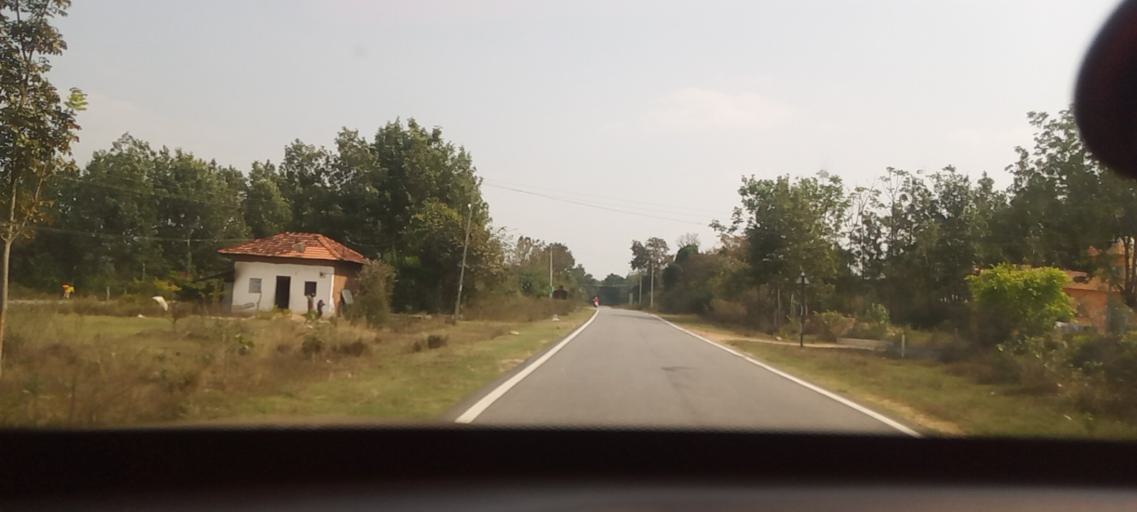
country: IN
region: Karnataka
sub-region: Hassan
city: Belur
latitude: 13.1783
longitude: 75.8102
